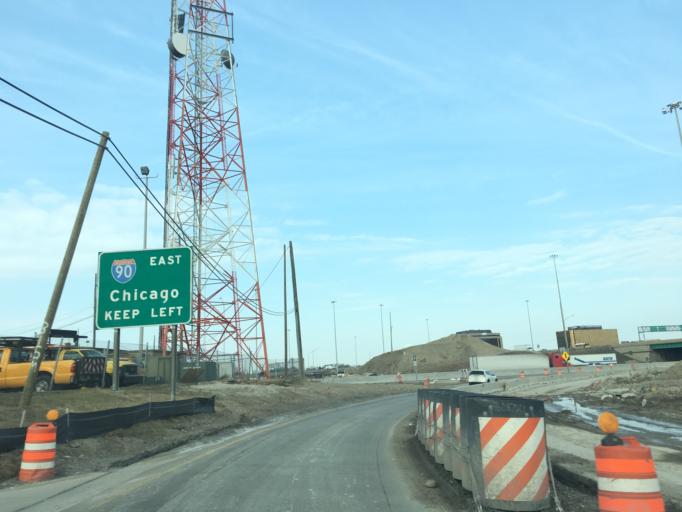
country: US
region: Illinois
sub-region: Cook County
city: Rolling Meadows
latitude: 42.0568
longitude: -88.0311
